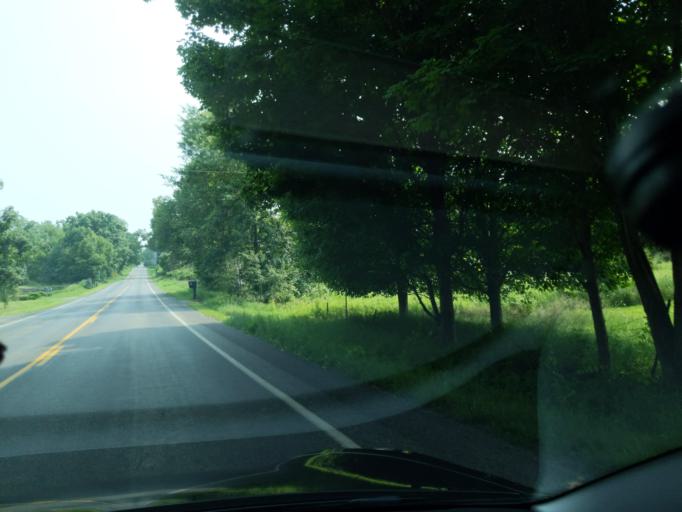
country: US
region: Michigan
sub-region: Eaton County
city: Eaton Rapids
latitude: 42.4817
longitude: -84.5609
